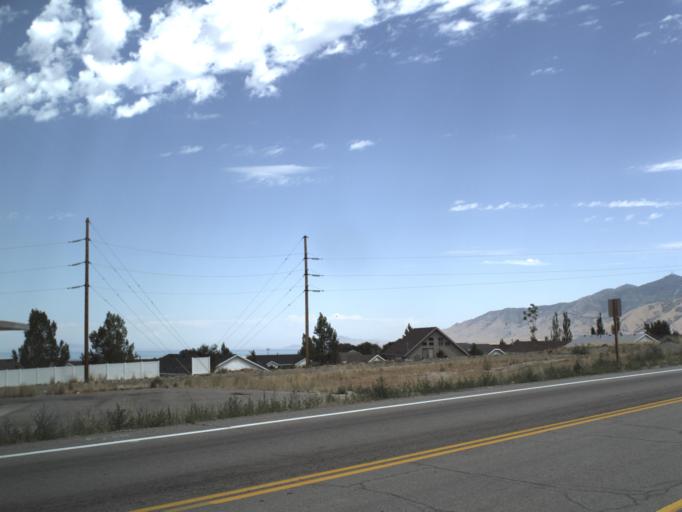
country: US
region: Utah
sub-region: Tooele County
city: Tooele
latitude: 40.5117
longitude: -112.3123
